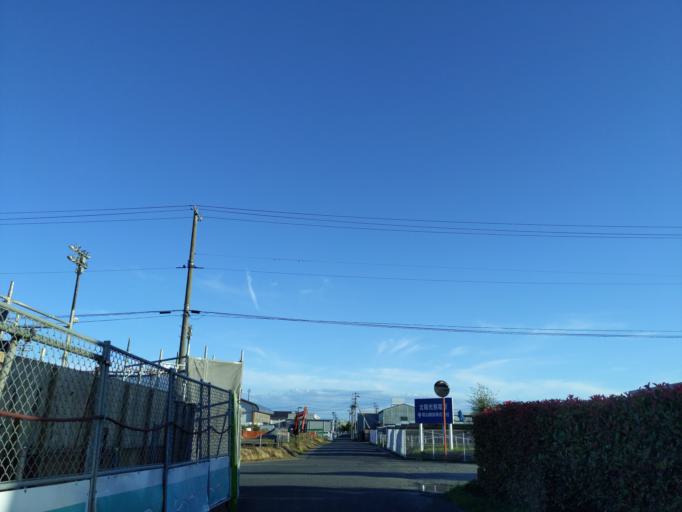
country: JP
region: Fukushima
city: Koriyama
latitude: 37.3785
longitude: 140.3925
